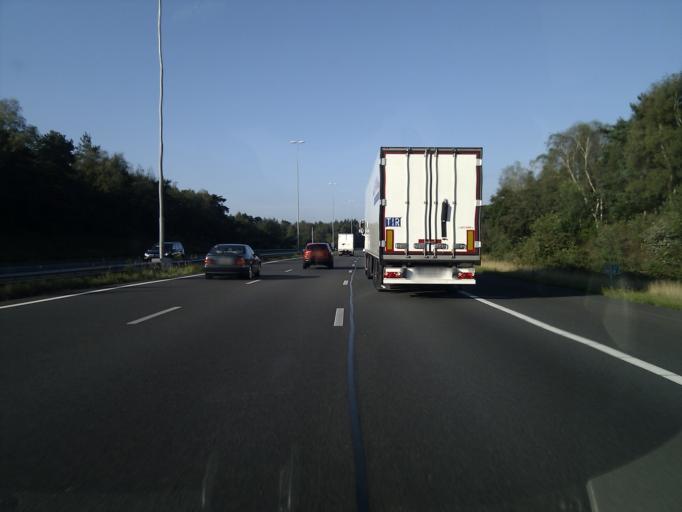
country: NL
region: Gelderland
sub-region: Gemeente Renkum
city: Wolfheze
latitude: 52.0024
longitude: 5.8045
